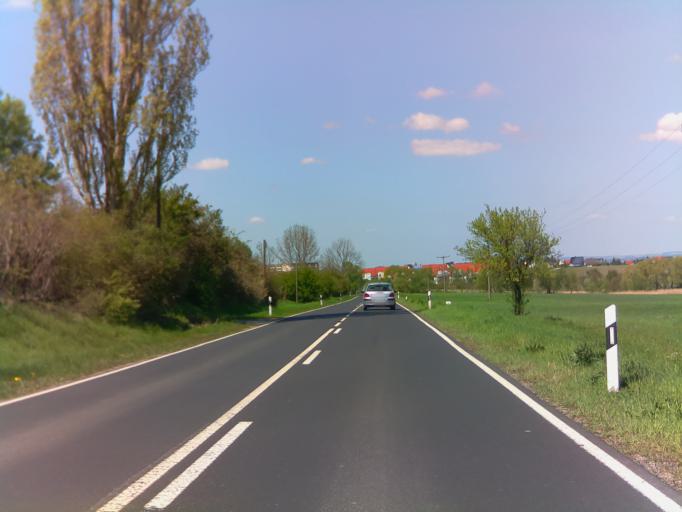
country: DE
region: Thuringia
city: Dornheim
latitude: 50.8166
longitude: 10.9695
